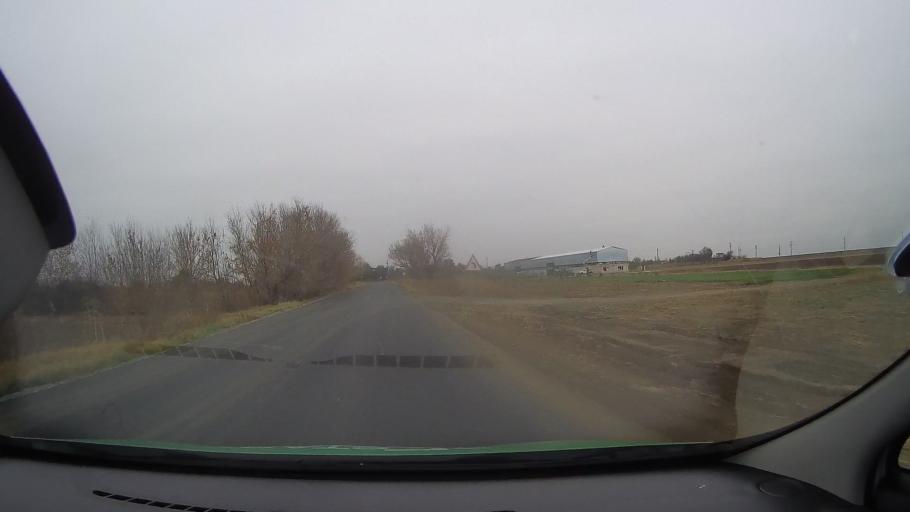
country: RO
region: Ialomita
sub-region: Comuna Valea Ciorii
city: Valea Ciorii
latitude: 44.7391
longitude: 27.5775
